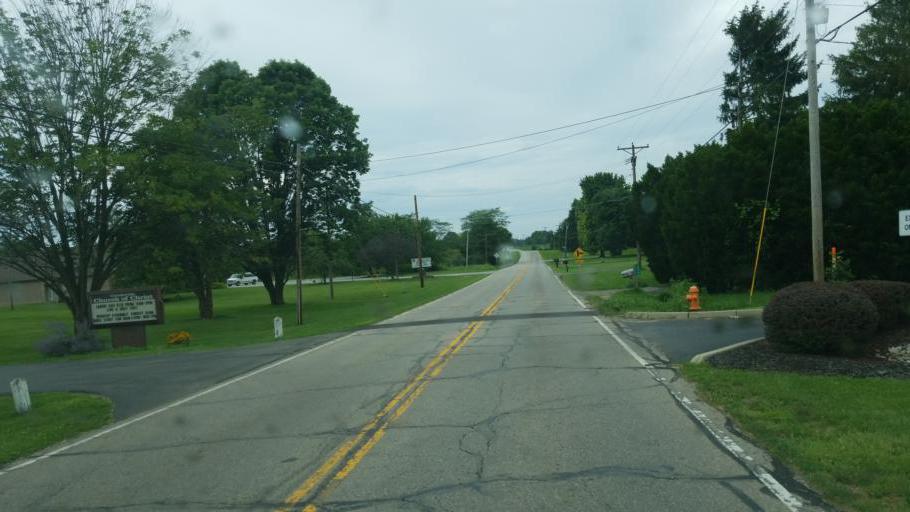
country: US
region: Ohio
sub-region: Pickaway County
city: Circleville
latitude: 39.6288
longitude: -82.9434
